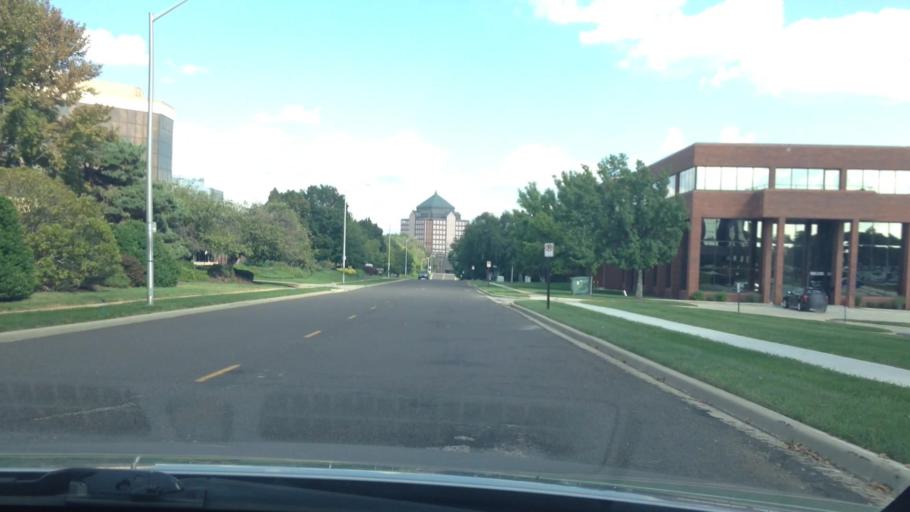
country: US
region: Kansas
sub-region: Johnson County
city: Overland Park
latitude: 38.9290
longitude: -94.6822
